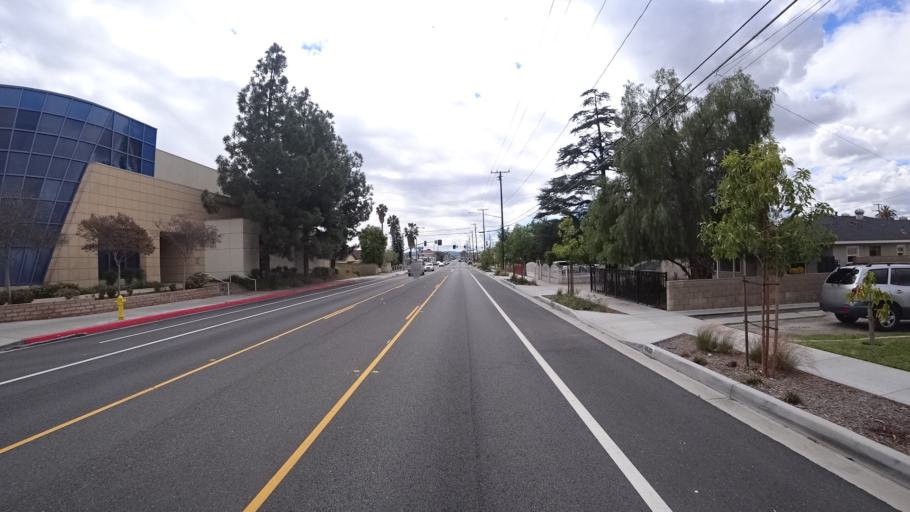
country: US
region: California
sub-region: Los Angeles County
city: Baldwin Park
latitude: 34.0966
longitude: -117.9605
